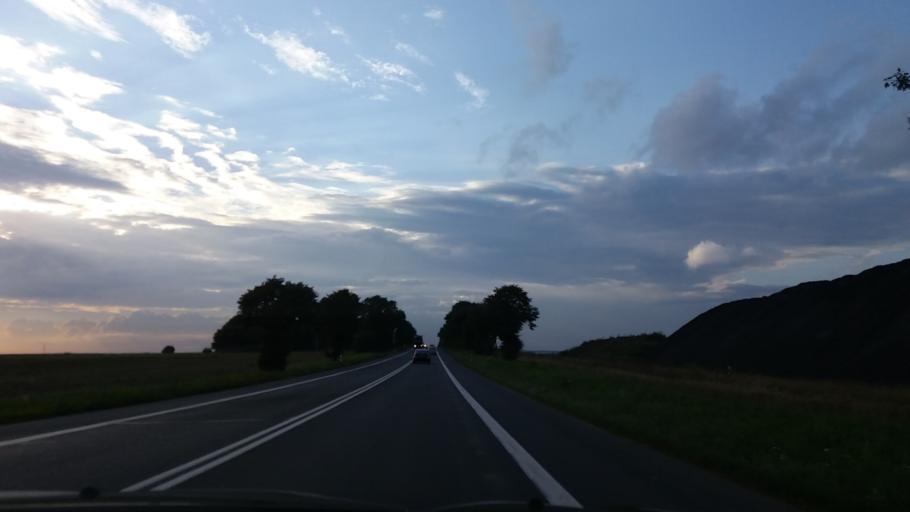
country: PL
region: Lower Silesian Voivodeship
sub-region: Powiat polkowicki
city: Radwanice
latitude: 51.6013
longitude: 15.9574
